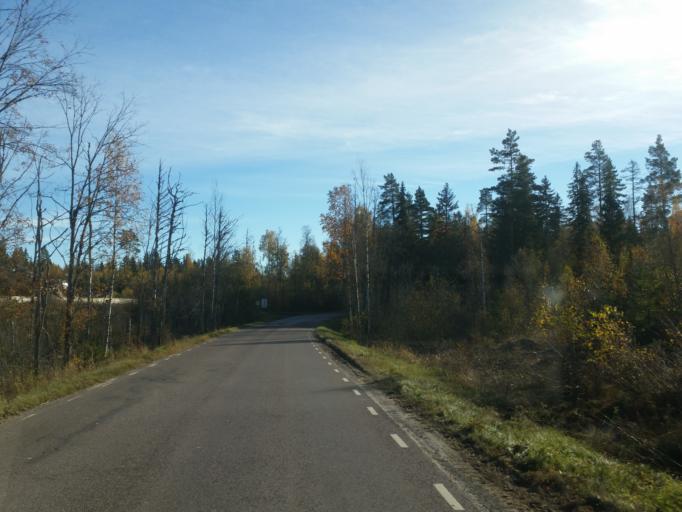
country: SE
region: Dalarna
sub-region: Borlange Kommun
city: Ornas
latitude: 60.5164
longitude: 15.5207
